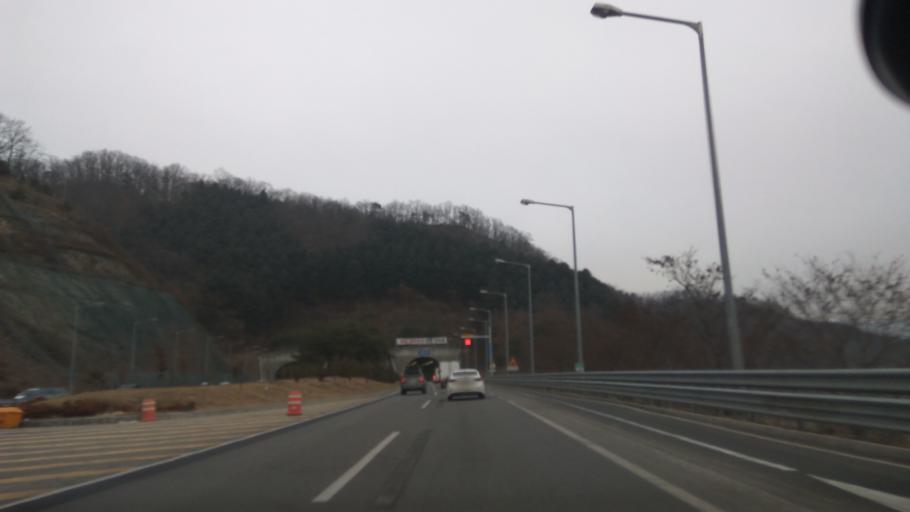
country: KR
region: Gangwon-do
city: Sindong
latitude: 37.7424
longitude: 127.6811
